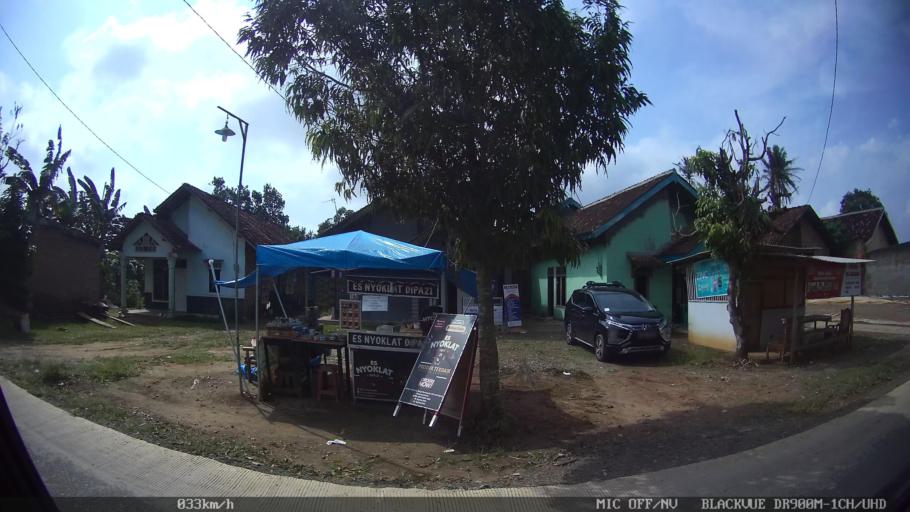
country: ID
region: Lampung
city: Kedaton
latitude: -5.3324
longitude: 105.2809
